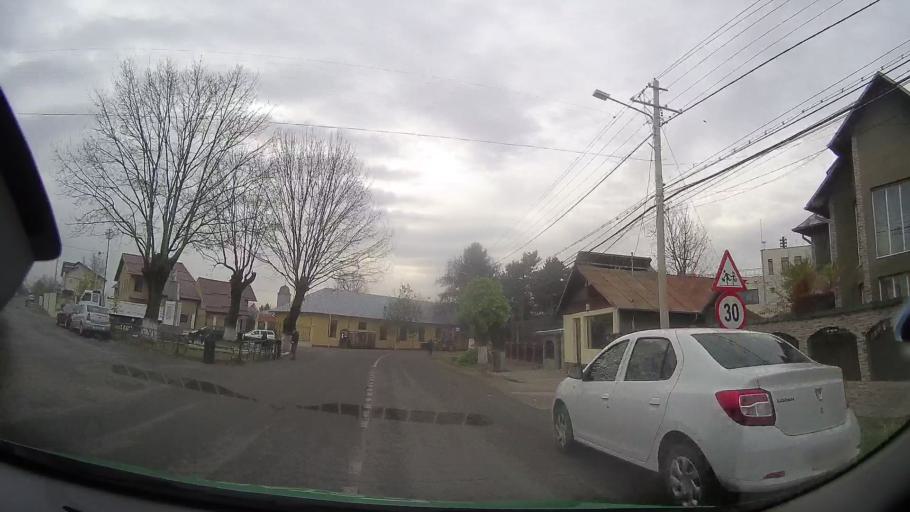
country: RO
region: Prahova
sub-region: Comuna Berceni
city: Berceni
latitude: 44.9319
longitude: 26.1231
